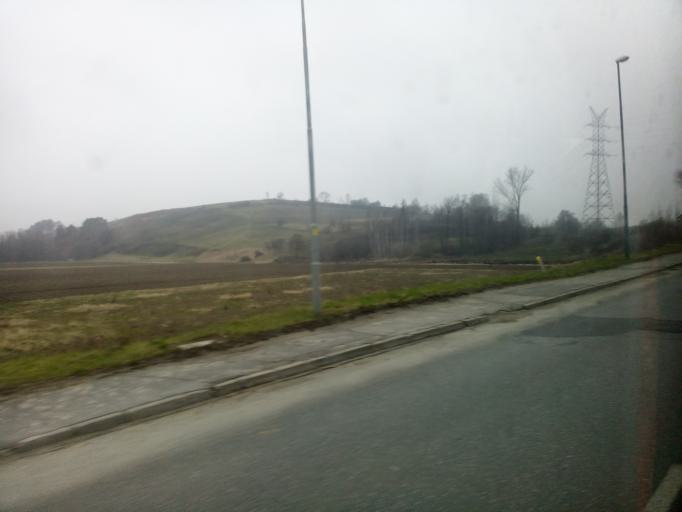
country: PL
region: Lesser Poland Voivodeship
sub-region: Powiat nowosadecki
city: Stary Sacz
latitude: 49.5738
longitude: 20.6628
